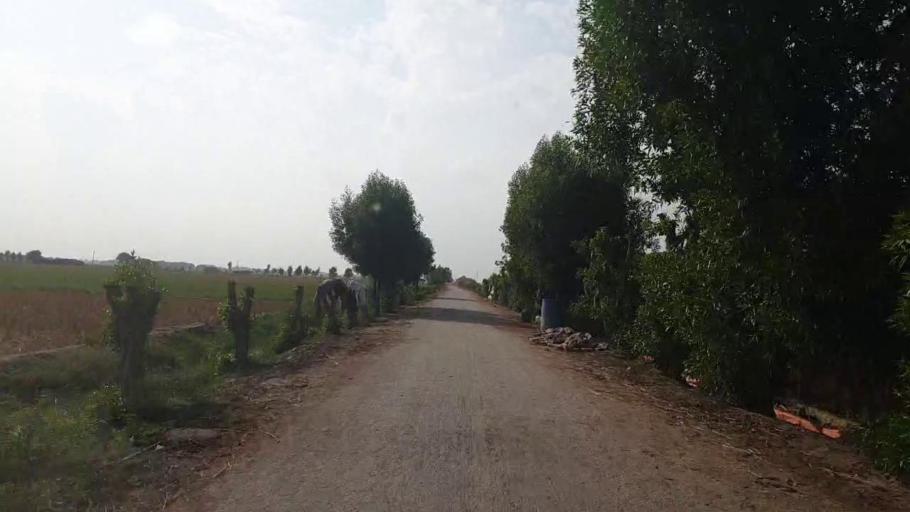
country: PK
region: Sindh
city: Kario
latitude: 24.6404
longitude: 68.5615
